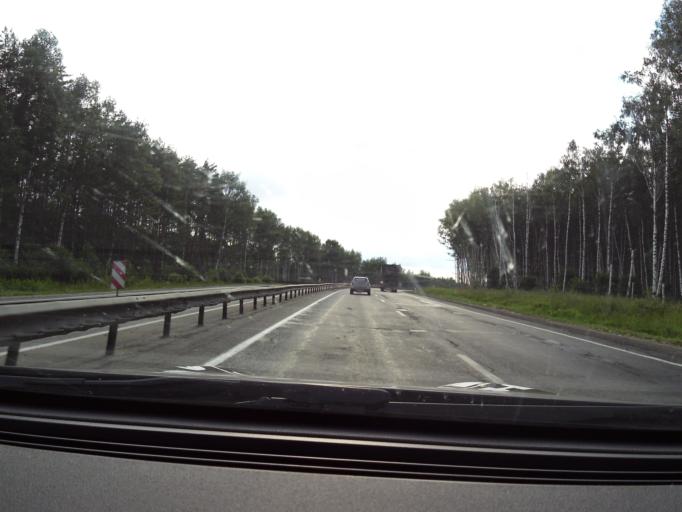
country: RU
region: Vladimir
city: Novovyazniki
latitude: 56.2033
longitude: 42.2958
